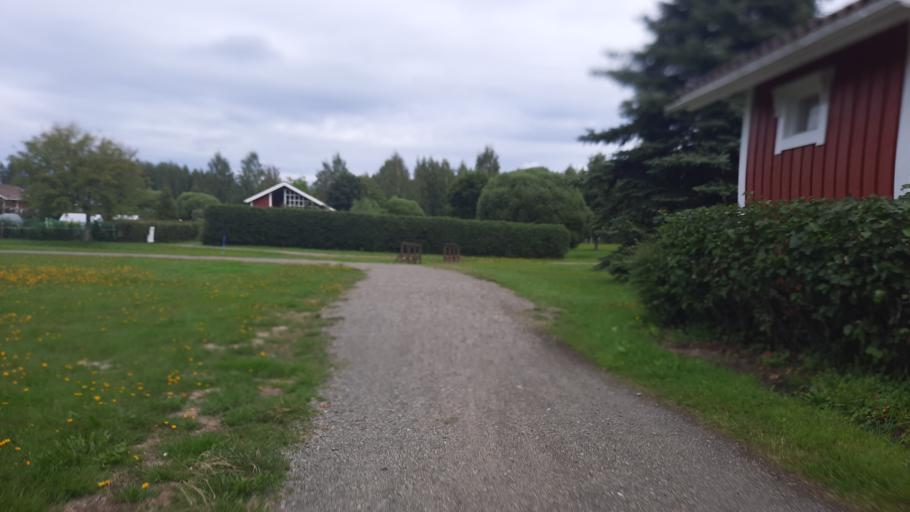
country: FI
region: North Karelia
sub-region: Joensuu
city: Joensuu
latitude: 62.6131
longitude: 29.8487
